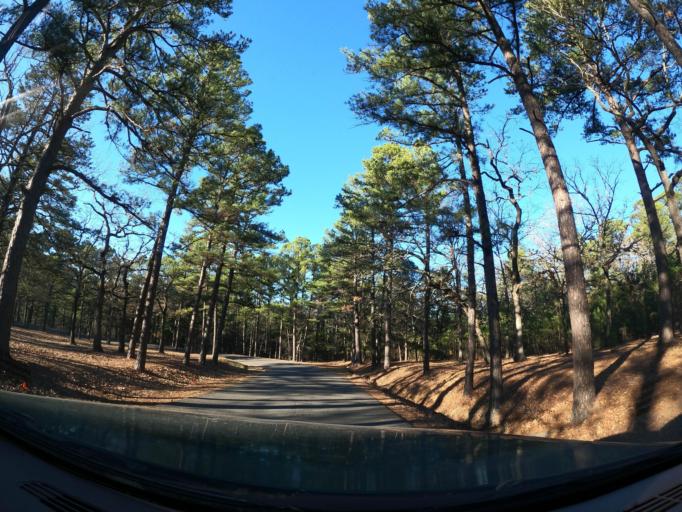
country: US
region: Oklahoma
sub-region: Latimer County
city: Wilburton
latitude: 34.9815
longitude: -95.3573
